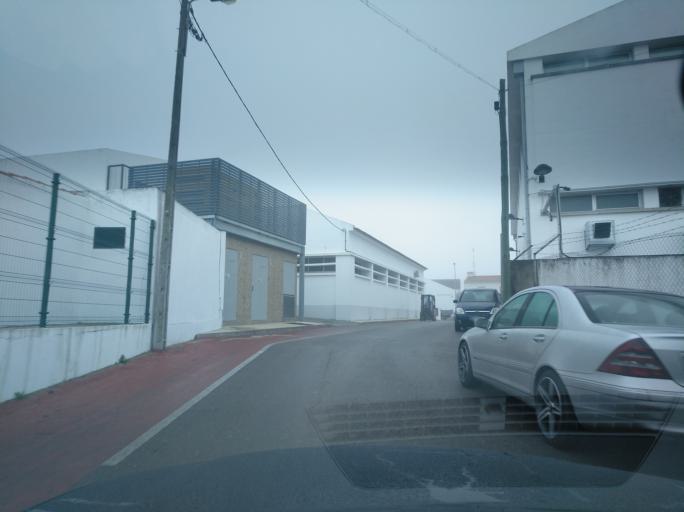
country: PT
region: Portalegre
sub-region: Campo Maior
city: Campo Maior
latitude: 39.0214
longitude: -7.0683
